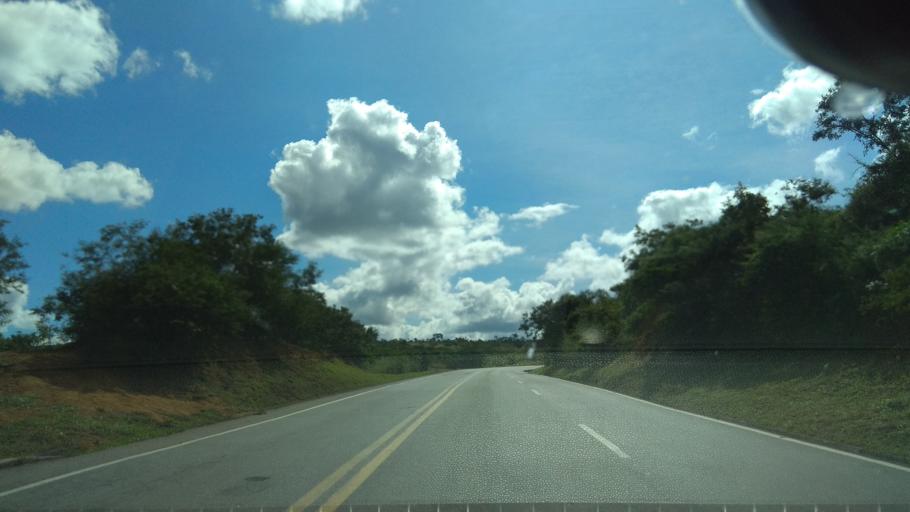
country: BR
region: Bahia
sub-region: Santa Ines
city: Santa Ines
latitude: -13.2215
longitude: -40.0277
